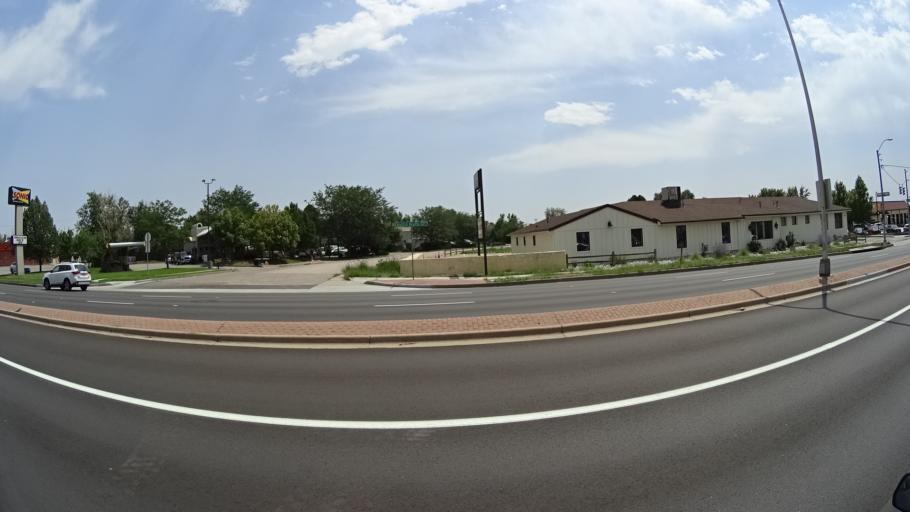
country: US
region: Colorado
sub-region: El Paso County
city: Cimarron Hills
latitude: 38.8956
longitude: -104.7486
